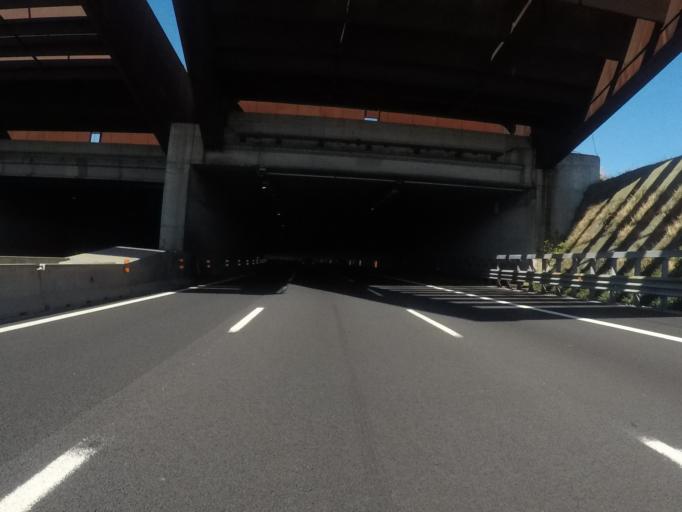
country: IT
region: Tuscany
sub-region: Province of Florence
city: Mantignano-Ugnano
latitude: 43.7624
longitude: 11.1695
